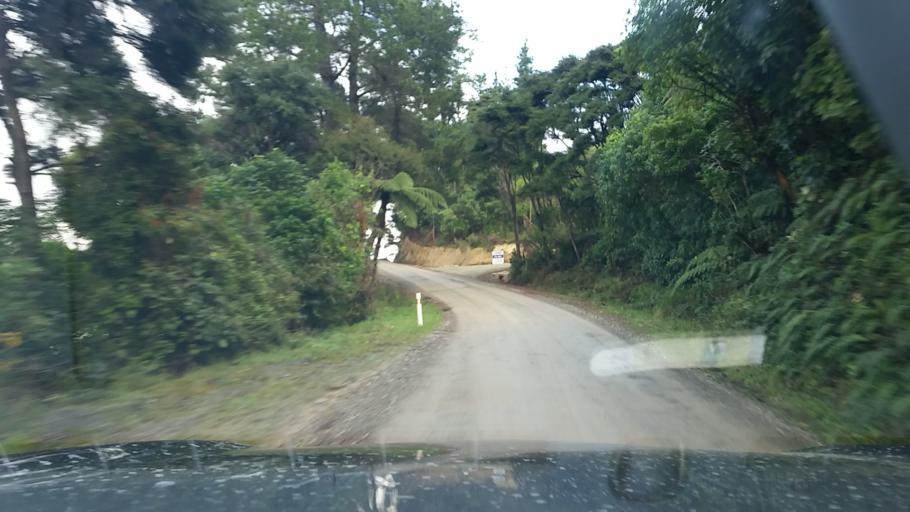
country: NZ
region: Marlborough
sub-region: Marlborough District
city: Picton
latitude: -41.1778
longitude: 174.0662
